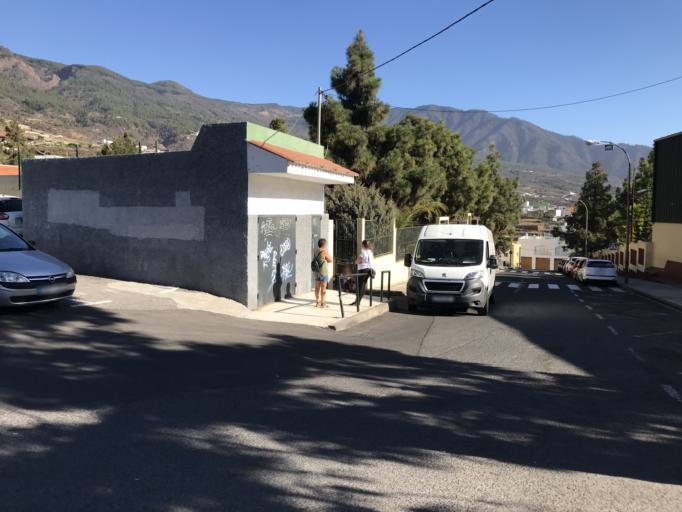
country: ES
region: Canary Islands
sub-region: Provincia de Santa Cruz de Tenerife
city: Arafo
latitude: 28.3335
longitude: -16.4229
